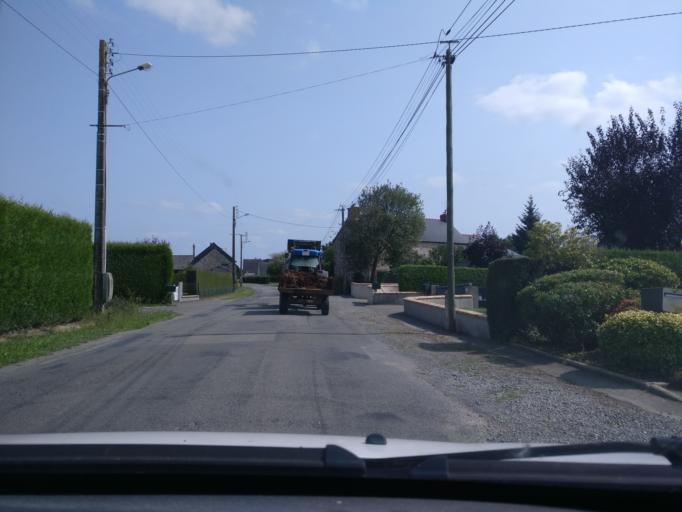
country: FR
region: Brittany
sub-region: Departement d'Ille-et-Vilaine
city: Gosne
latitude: 48.2487
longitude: -1.4717
